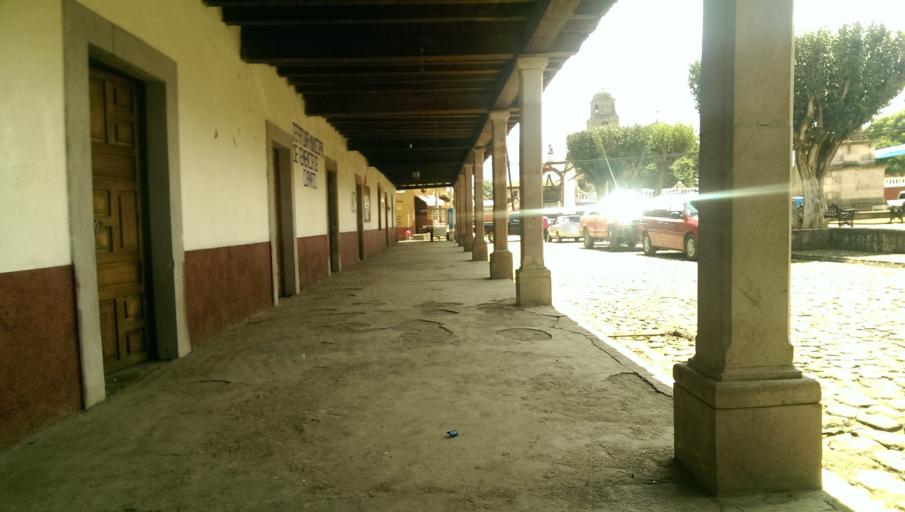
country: MX
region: Michoacan
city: Cuanajo
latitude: 19.4855
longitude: -101.5092
